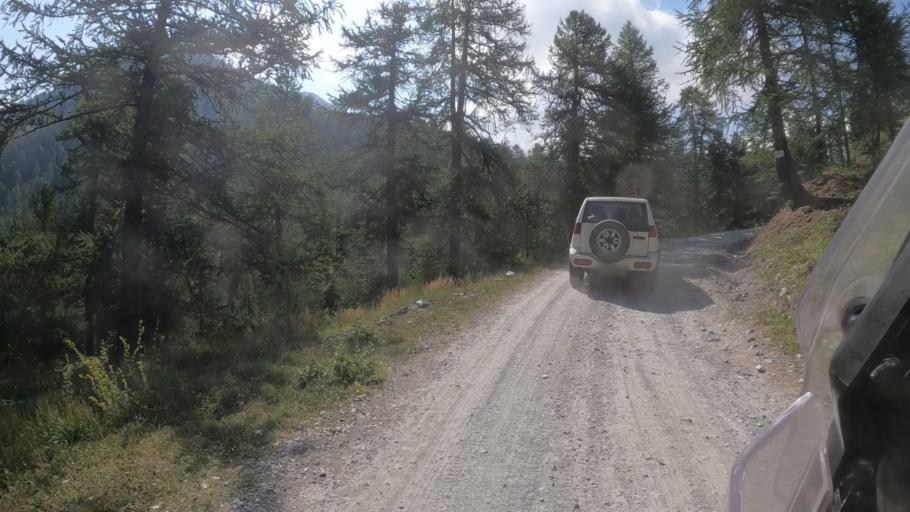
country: IT
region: Piedmont
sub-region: Provincia di Torino
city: Cesana Torinese
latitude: 44.9073
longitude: 6.7992
